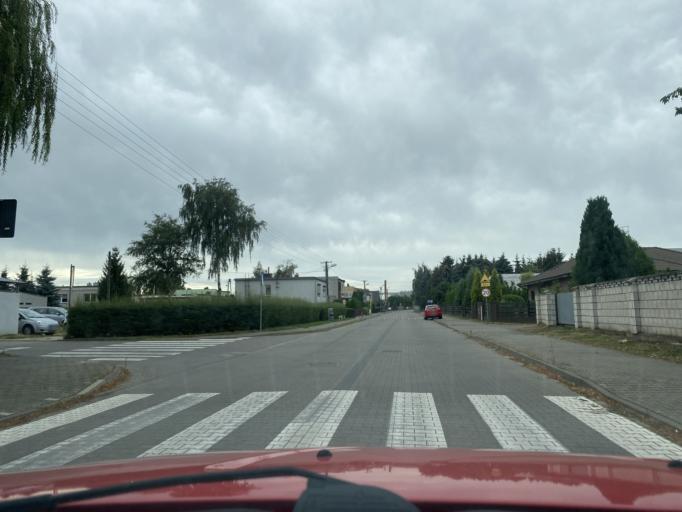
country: PL
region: Greater Poland Voivodeship
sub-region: Powiat poznanski
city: Tarnowo Podgorne
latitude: 52.4621
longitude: 16.6565
